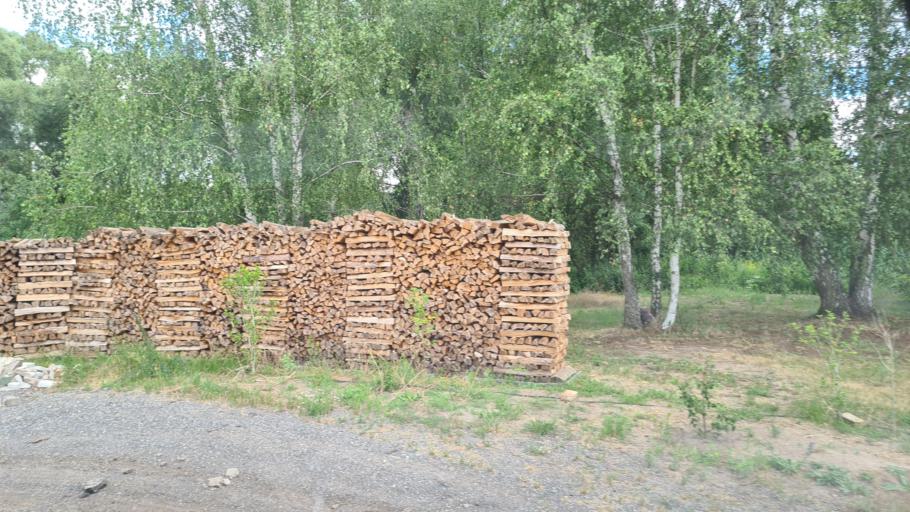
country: DE
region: Brandenburg
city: Luckenwalde
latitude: 52.1010
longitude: 13.1877
